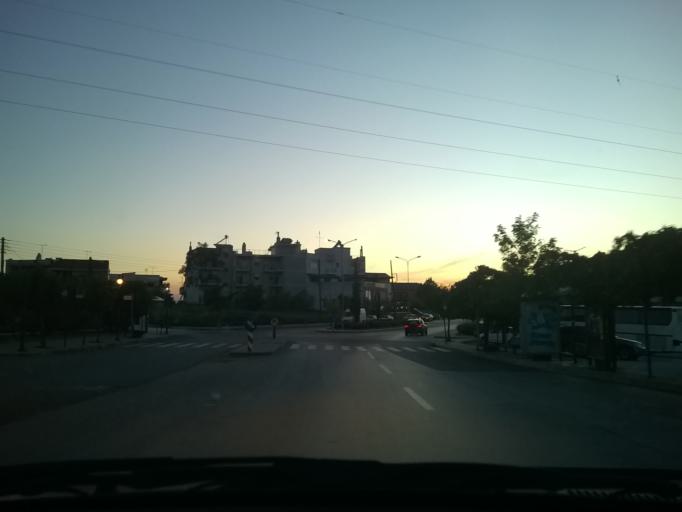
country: GR
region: Central Macedonia
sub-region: Nomos Thessalonikis
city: Polichni
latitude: 40.6653
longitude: 22.9526
